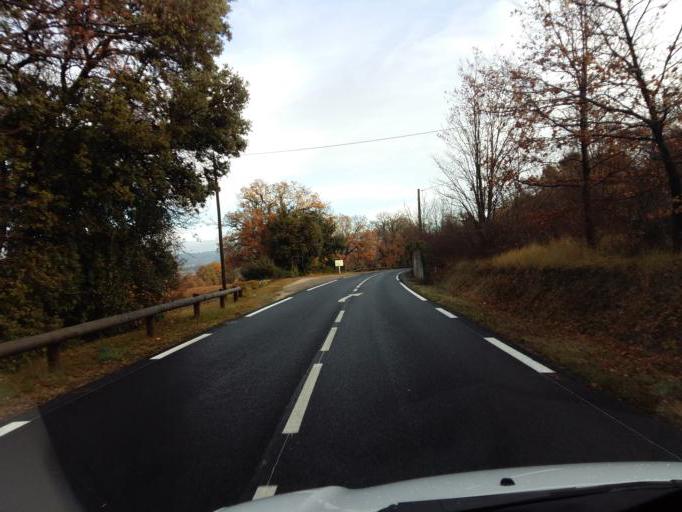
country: FR
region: Provence-Alpes-Cote d'Azur
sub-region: Departement du Vaucluse
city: Vaison-la-Romaine
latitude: 44.2405
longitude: 5.0311
